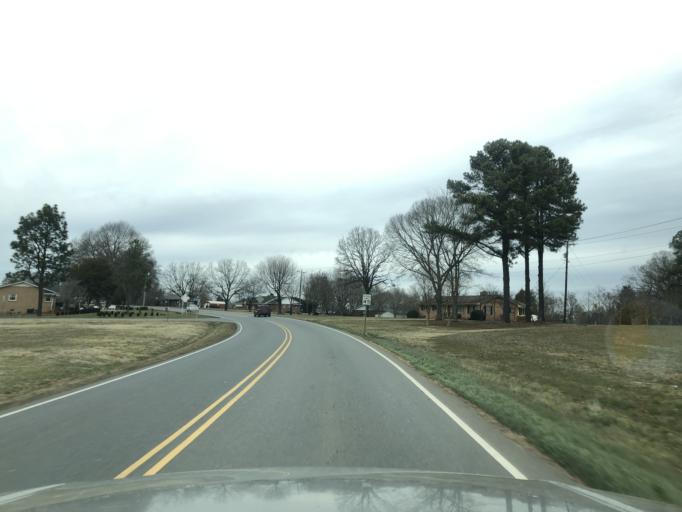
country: US
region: North Carolina
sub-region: Cleveland County
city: Shelby
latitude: 35.3258
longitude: -81.4951
